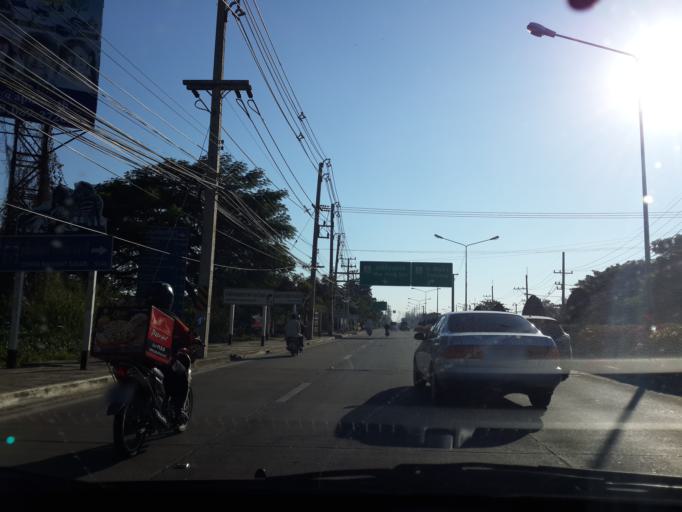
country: TH
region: Chiang Mai
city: Hang Dong
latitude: 18.7253
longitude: 98.9473
